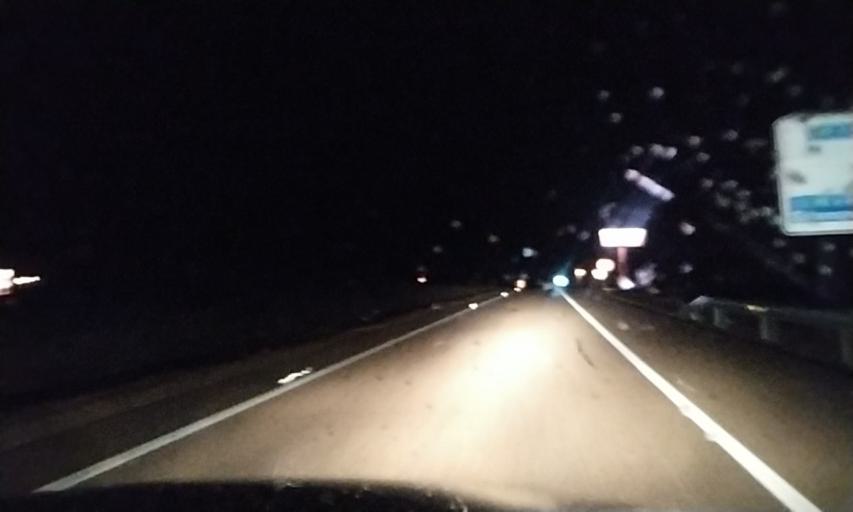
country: ES
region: Castille and Leon
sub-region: Provincia de Salamanca
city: Martin de Yeltes
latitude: 40.7723
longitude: -6.2850
